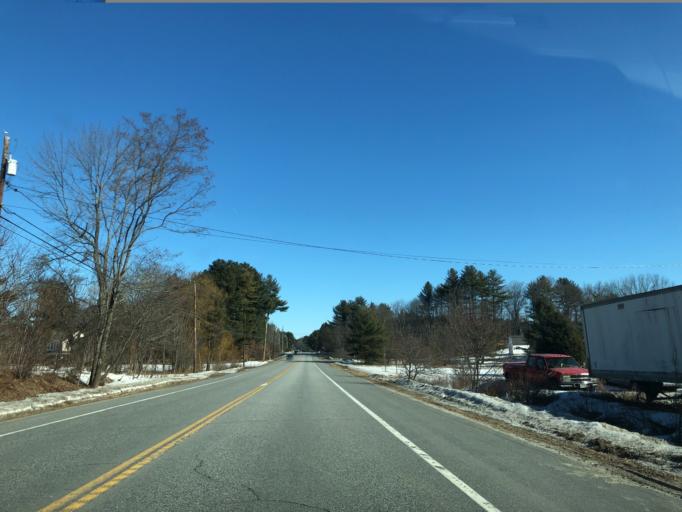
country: US
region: Maine
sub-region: Cumberland County
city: North Windham
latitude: 43.8172
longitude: -70.3961
